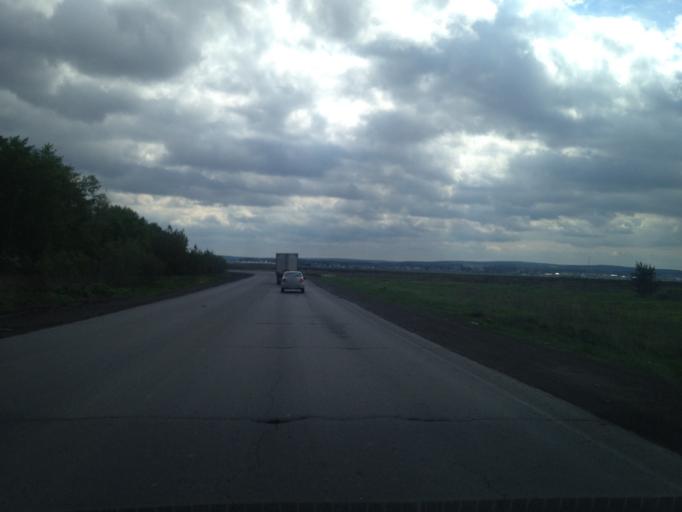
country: RU
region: Sverdlovsk
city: Aramil
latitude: 56.6942
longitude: 60.7604
